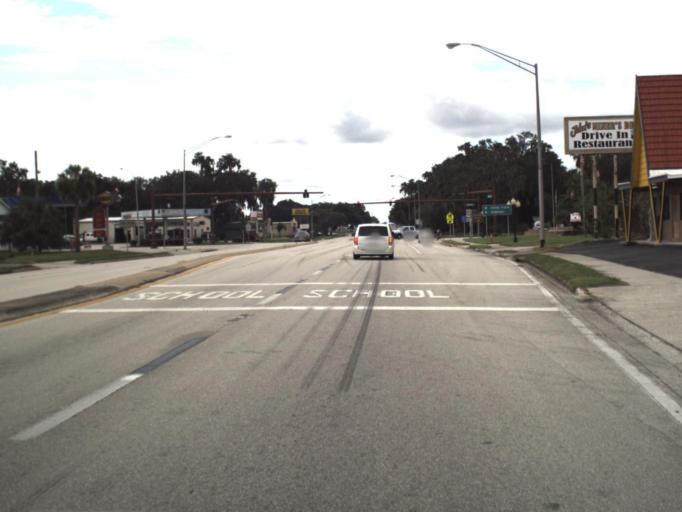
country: US
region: Florida
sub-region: Polk County
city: Fort Meade
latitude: 27.7532
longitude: -81.8016
